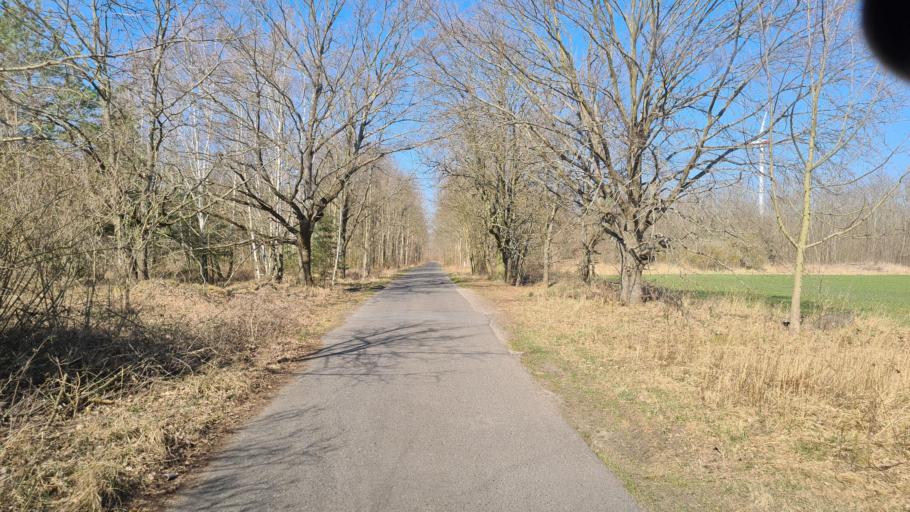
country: DE
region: Brandenburg
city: Calau
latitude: 51.7922
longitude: 13.9969
